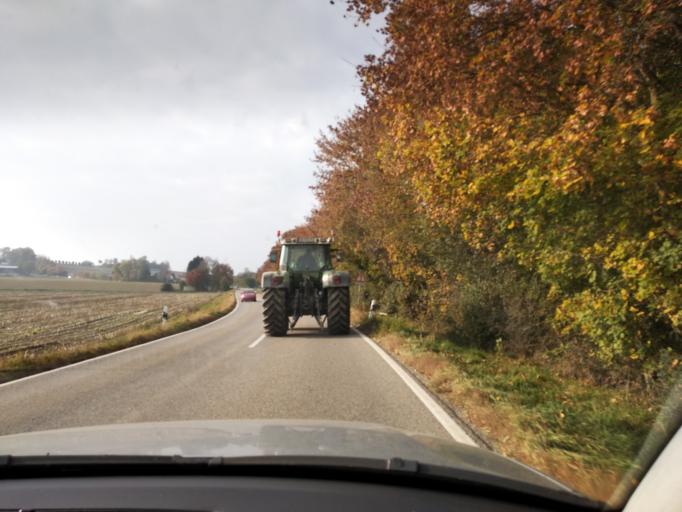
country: DE
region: Bavaria
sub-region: Upper Bavaria
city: Markt Schwaben
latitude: 48.1818
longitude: 11.8756
